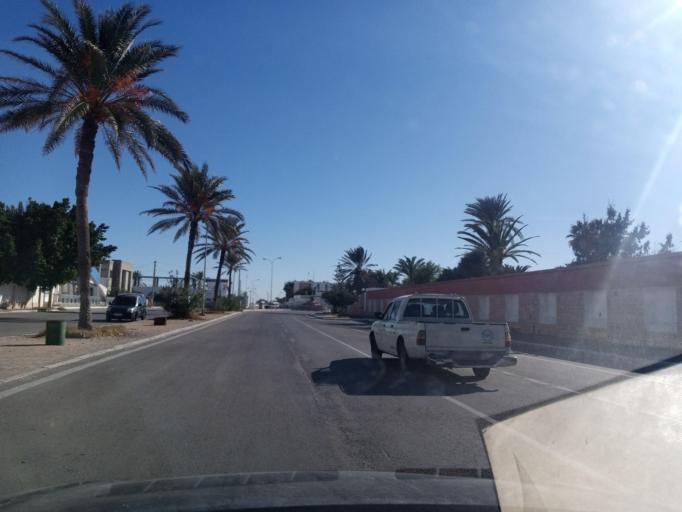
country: TN
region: Qabis
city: Gabes
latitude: 33.8936
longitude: 10.1145
